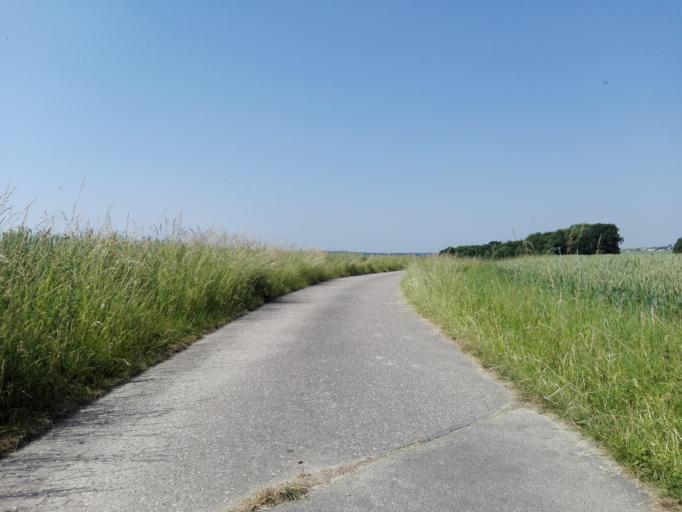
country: DE
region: Baden-Wuerttemberg
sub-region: Regierungsbezirk Stuttgart
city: Kuenzelsau
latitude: 49.3177
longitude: 9.7054
